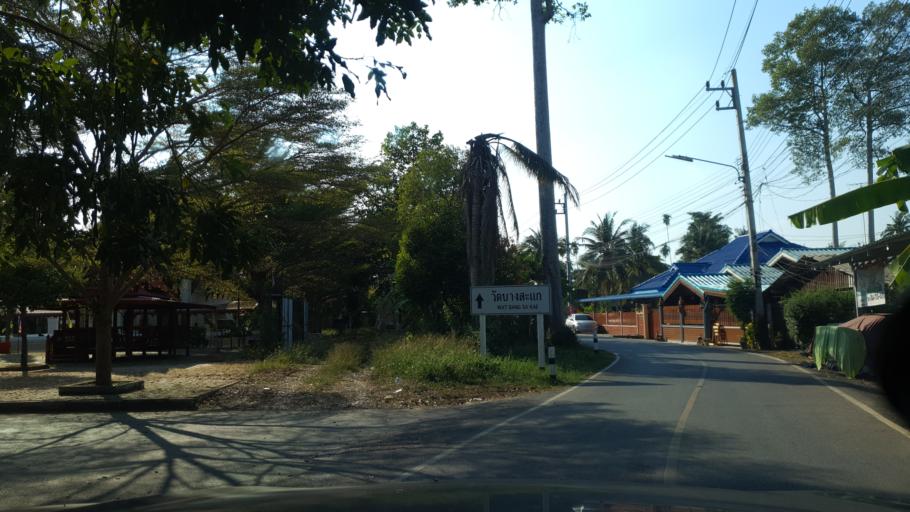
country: TH
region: Samut Songkhram
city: Amphawa
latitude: 13.4430
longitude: 99.9409
